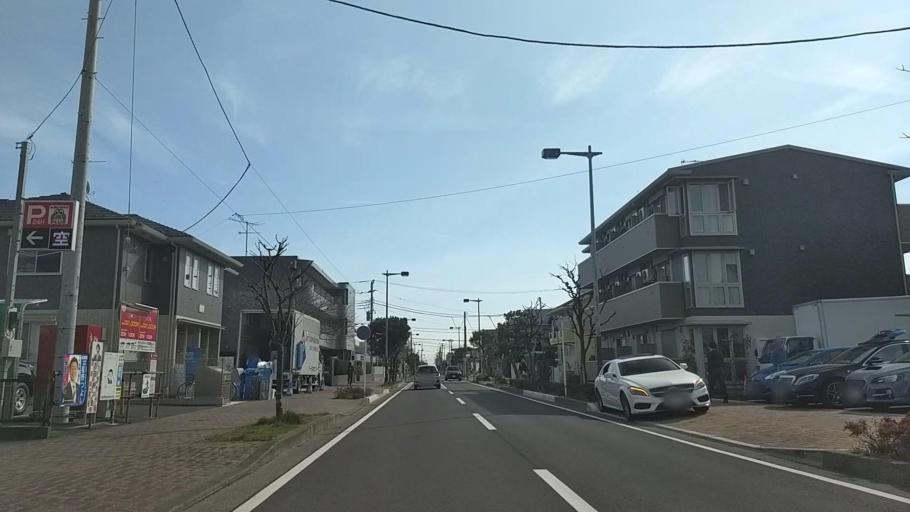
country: JP
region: Kanagawa
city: Fujisawa
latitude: 35.3324
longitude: 139.4473
